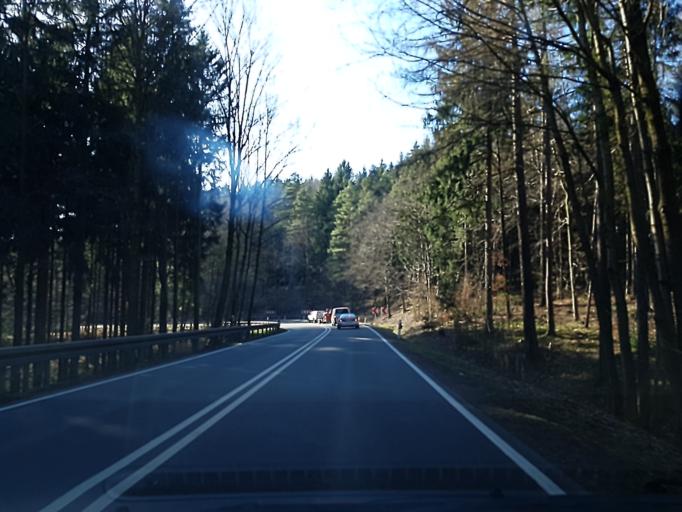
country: DE
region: Saxony
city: Falkenau
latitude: 50.8592
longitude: 13.1319
